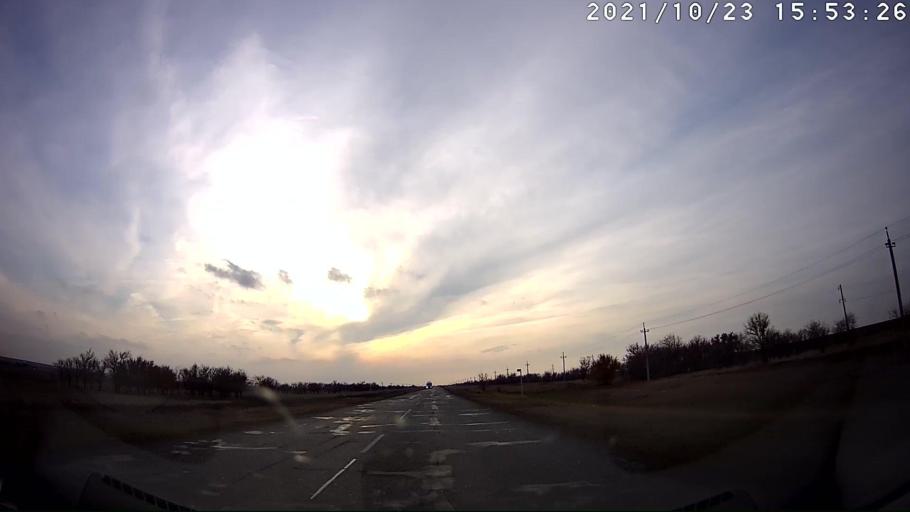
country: RU
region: Kalmykiya
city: Sadovoye
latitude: 47.9798
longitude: 43.9997
